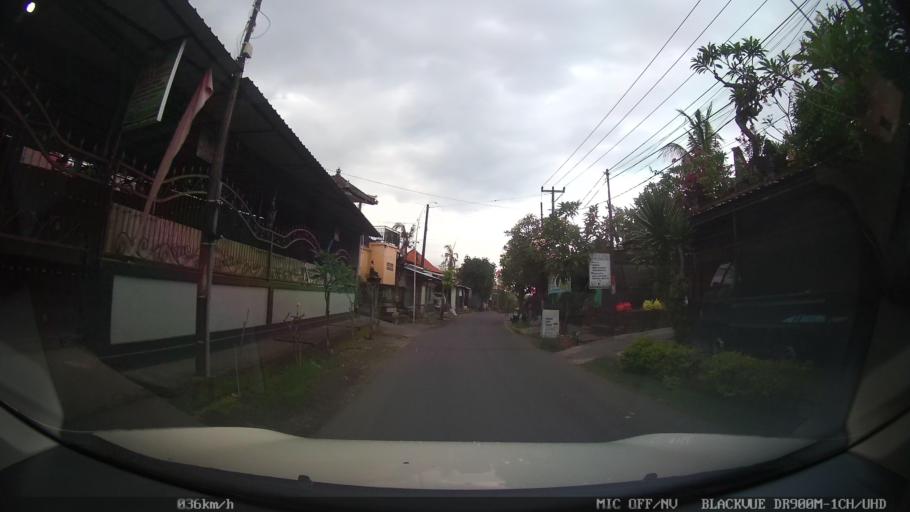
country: ID
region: Bali
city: Banjar Pasekan
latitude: -8.6289
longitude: 115.2876
